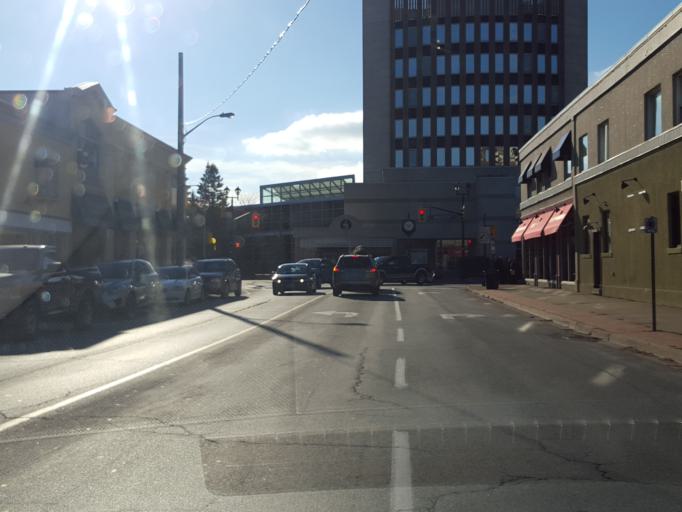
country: CA
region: Ontario
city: Burlington
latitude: 43.3264
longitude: -79.7977
